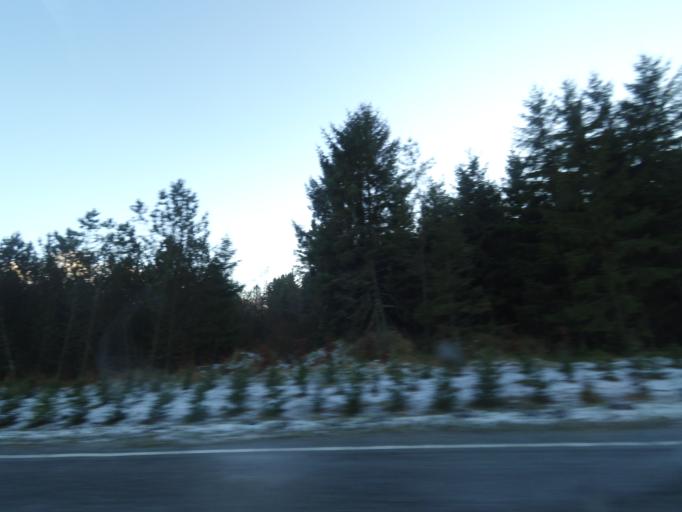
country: DK
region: Central Jutland
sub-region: Ikast-Brande Kommune
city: Brande
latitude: 56.0052
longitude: 9.1504
